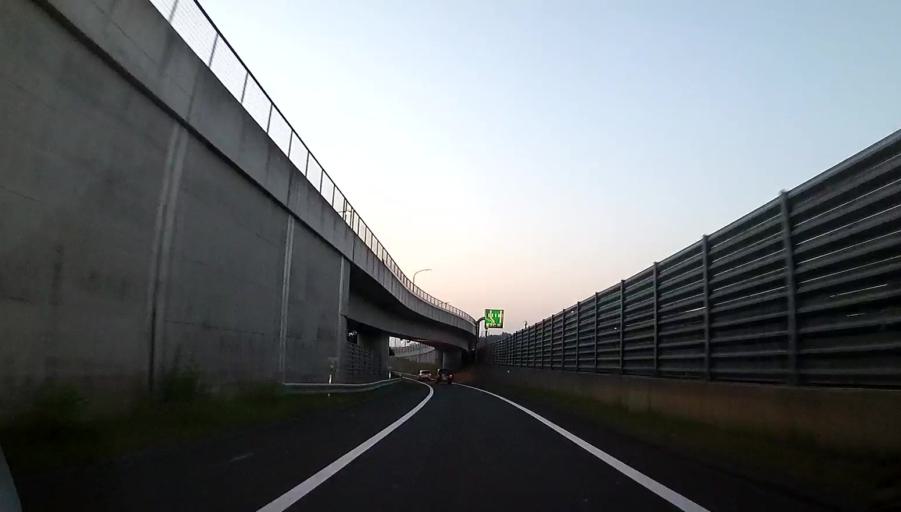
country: JP
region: Hokkaido
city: Kitahiroshima
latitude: 43.0121
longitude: 141.4651
